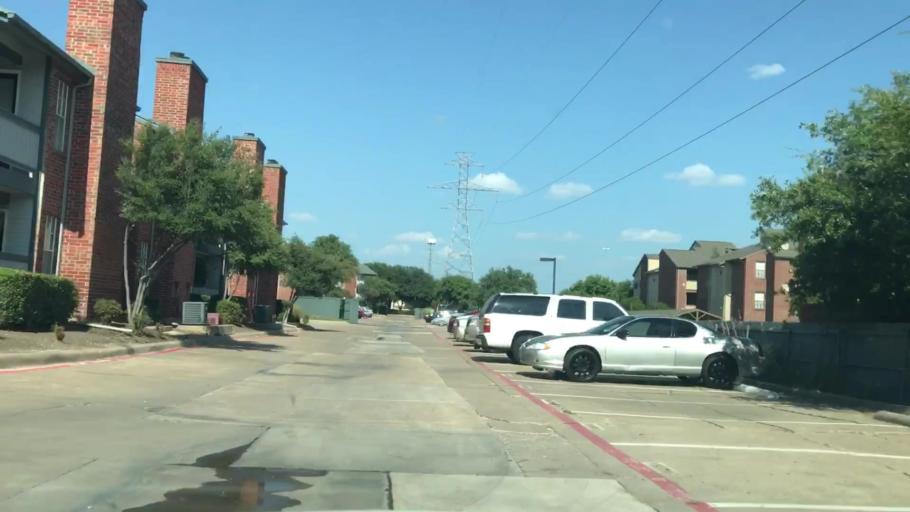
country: US
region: Texas
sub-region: Dallas County
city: Mesquite
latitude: 32.8180
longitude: -96.6342
